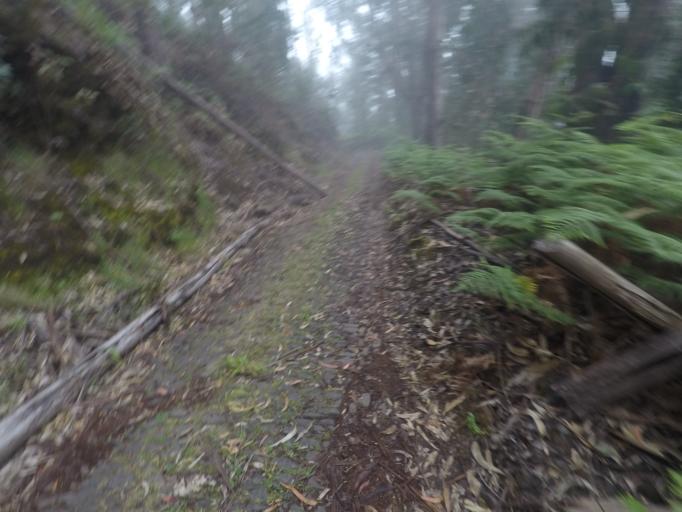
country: PT
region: Madeira
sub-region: Calheta
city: Arco da Calheta
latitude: 32.7272
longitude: -17.0961
